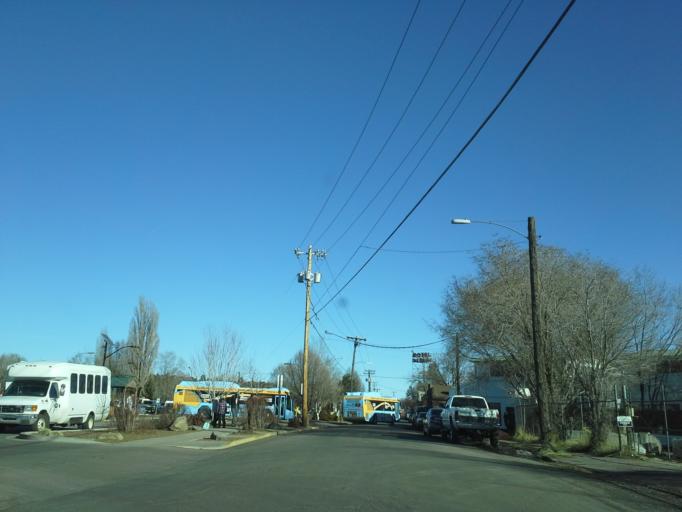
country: US
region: Arizona
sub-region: Coconino County
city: Flagstaff
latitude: 35.1973
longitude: -111.6531
